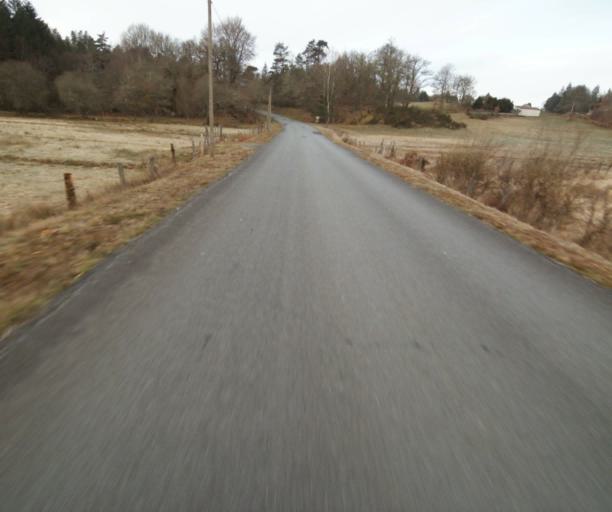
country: FR
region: Limousin
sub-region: Departement de la Correze
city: Correze
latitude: 45.4231
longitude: 1.8497
